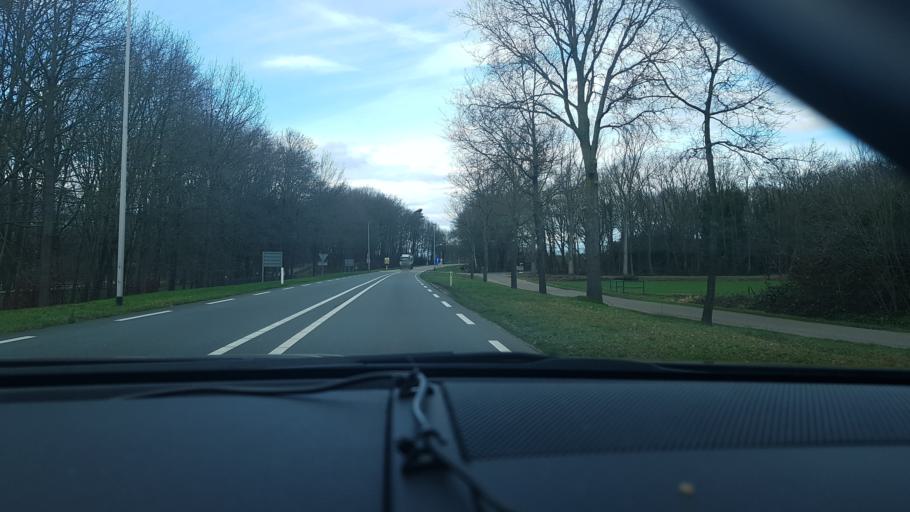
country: NL
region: Limburg
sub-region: Gemeente Beesel
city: Reuver
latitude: 51.3040
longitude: 6.0595
